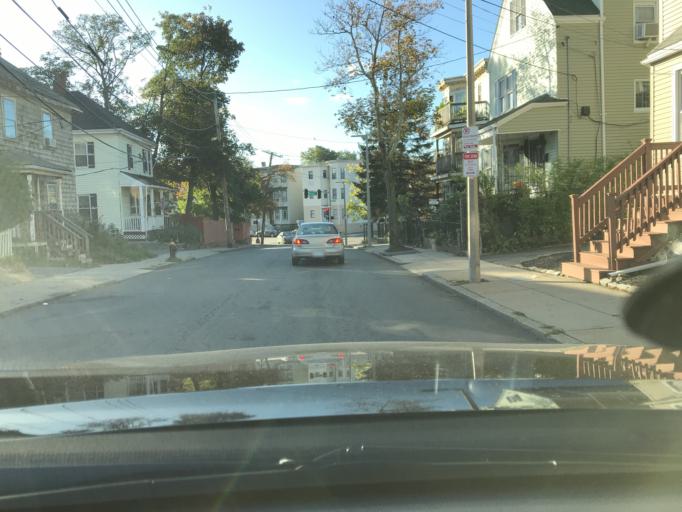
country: US
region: Massachusetts
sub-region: Norfolk County
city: Milton
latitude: 42.2925
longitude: -71.0775
